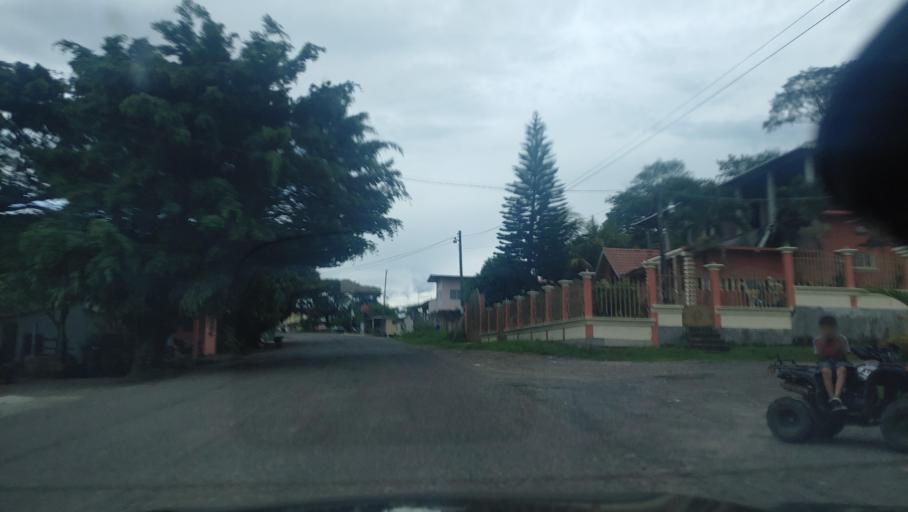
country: HN
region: Choluteca
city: Corpus
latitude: 13.3611
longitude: -86.9894
